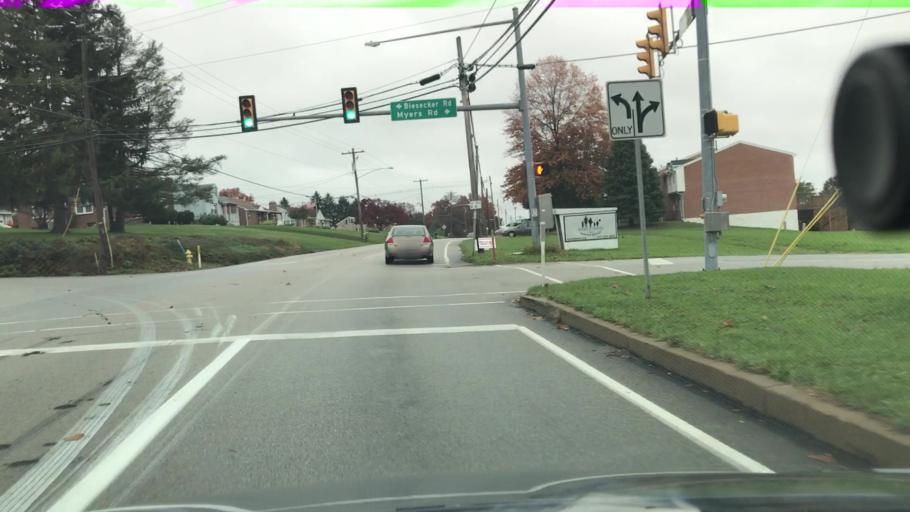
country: US
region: Pennsylvania
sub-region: York County
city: Spring Grove
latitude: 39.9103
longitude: -76.8421
